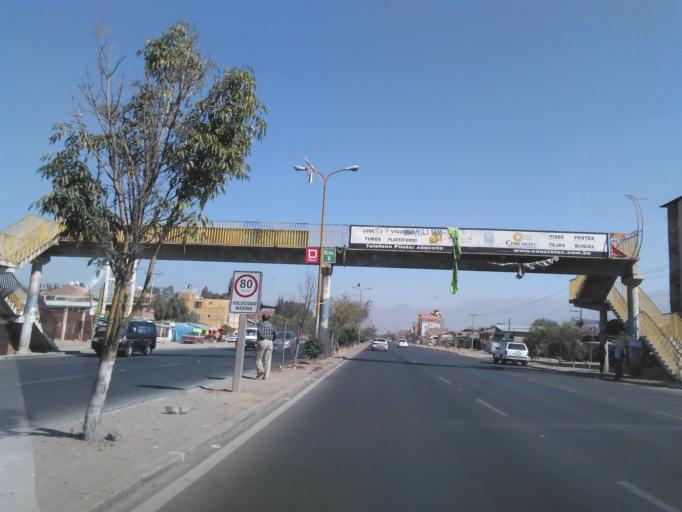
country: BO
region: Cochabamba
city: Cochabamba
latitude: -17.3912
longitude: -66.2317
